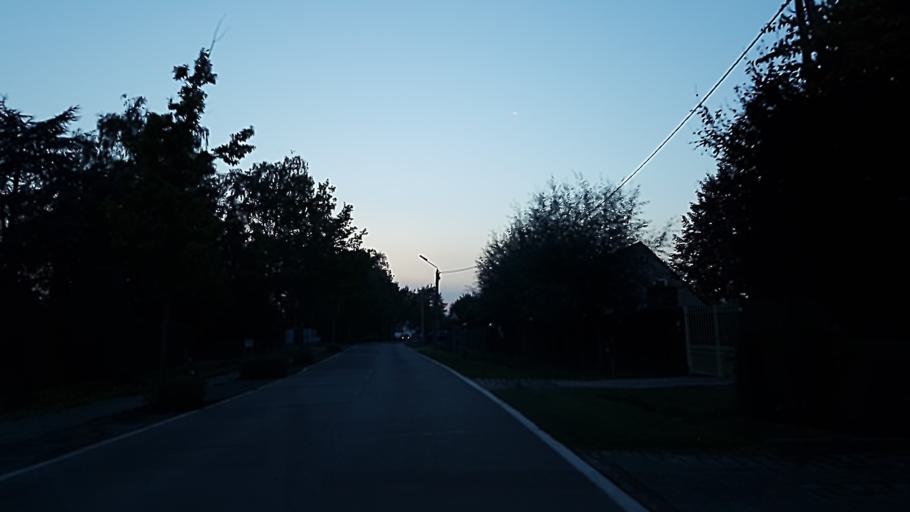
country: BE
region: Flanders
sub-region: Provincie Antwerpen
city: Rumst
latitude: 51.0795
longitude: 4.4593
